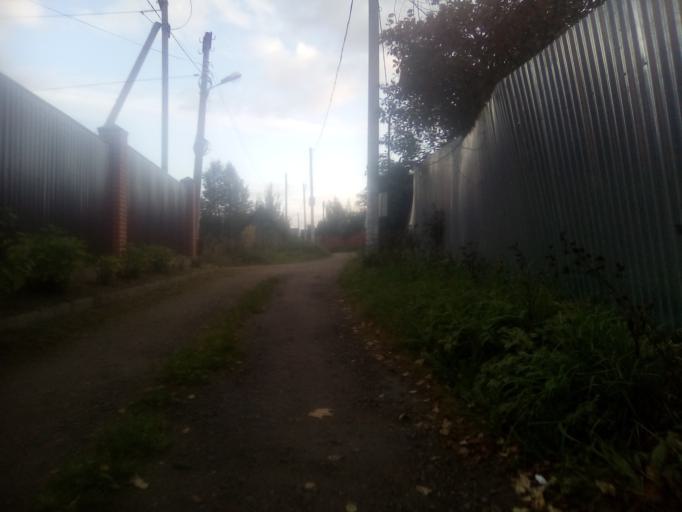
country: RU
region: Moskovskaya
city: Golitsyno
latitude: 55.5683
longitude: 37.0007
